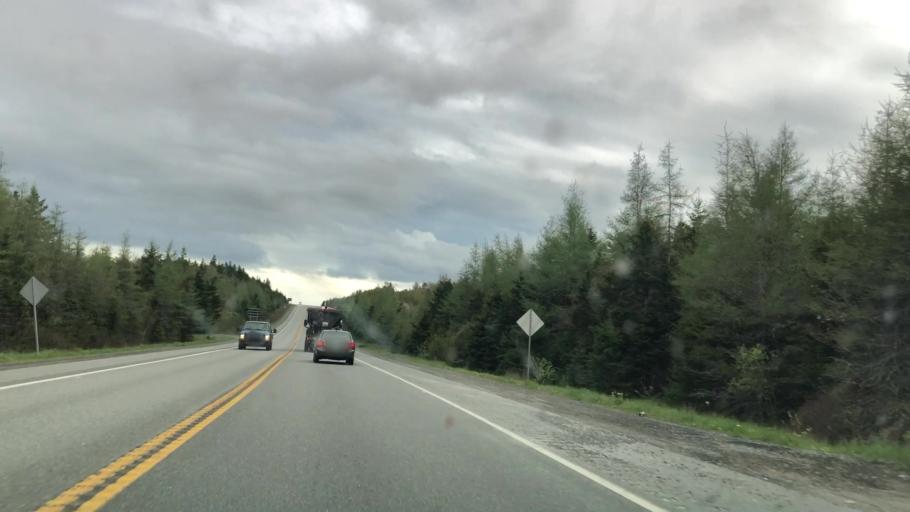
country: CA
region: Nova Scotia
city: Cole Harbour
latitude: 44.7805
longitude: -63.1777
